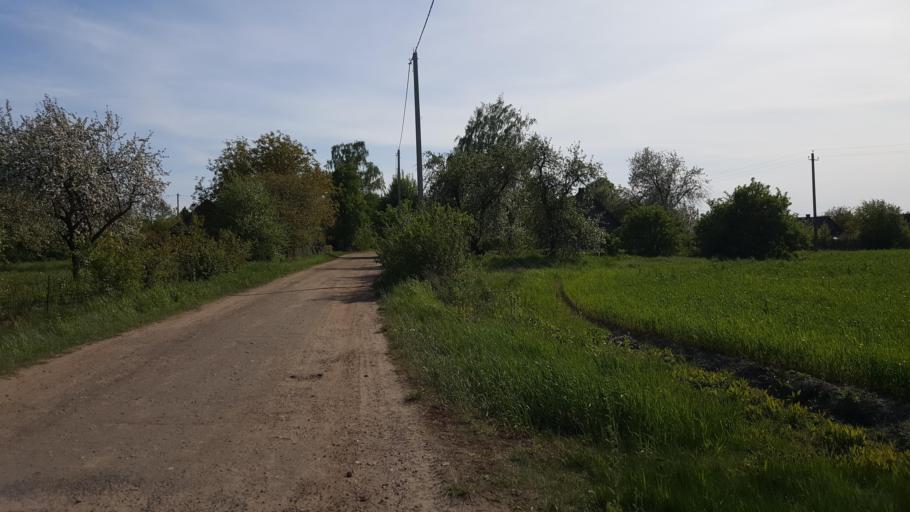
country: BY
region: Brest
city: Zhabinka
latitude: 52.3160
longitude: 23.9493
